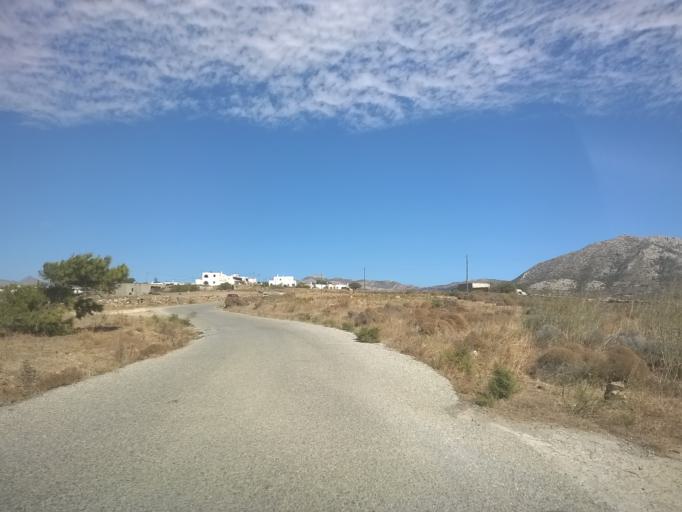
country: GR
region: South Aegean
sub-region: Nomos Kykladon
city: Filotion
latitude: 37.0377
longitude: 25.4306
